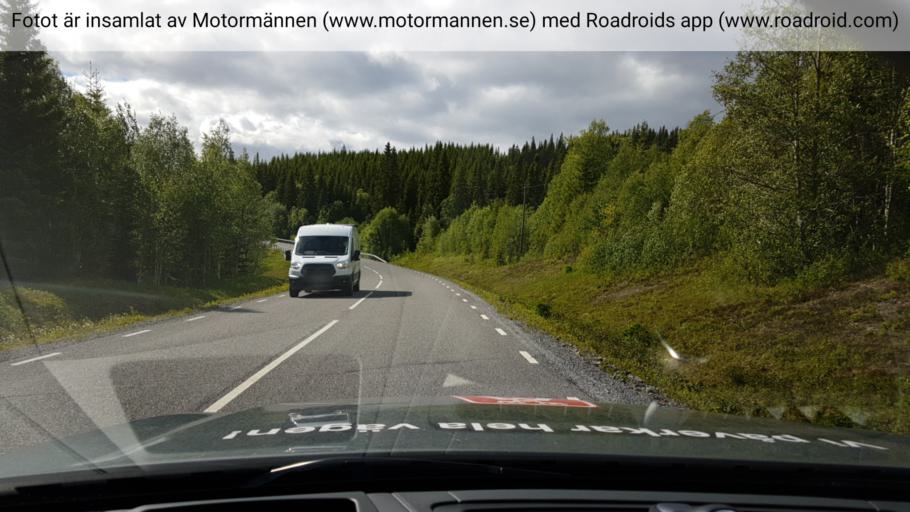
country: SE
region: Jaemtland
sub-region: Are Kommun
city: Are
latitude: 63.6229
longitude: 13.1564
